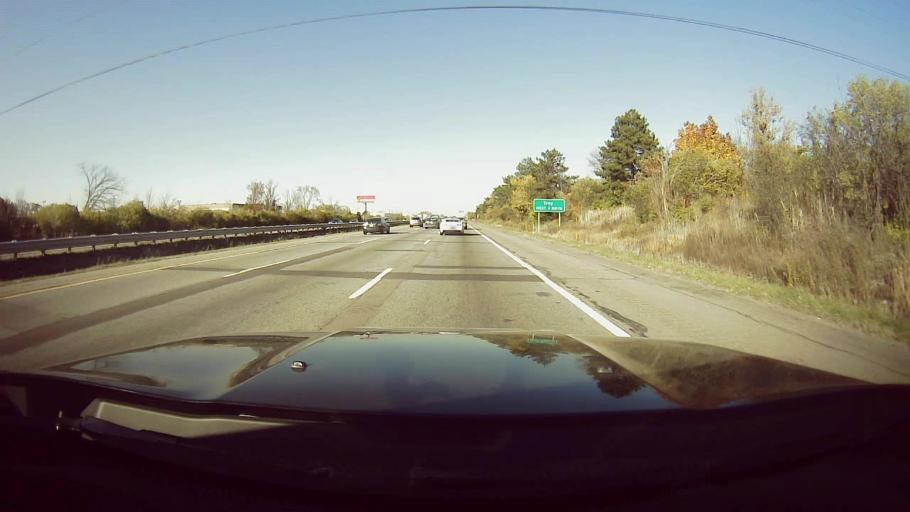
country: US
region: Michigan
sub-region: Oakland County
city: Madison Heights
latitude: 42.5133
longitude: -83.1150
